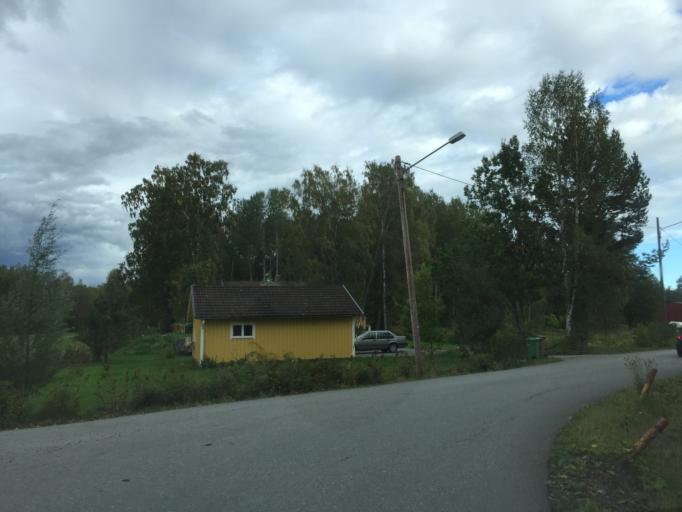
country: SE
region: OErebro
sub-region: Orebro Kommun
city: Hovsta
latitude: 59.3228
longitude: 15.2031
